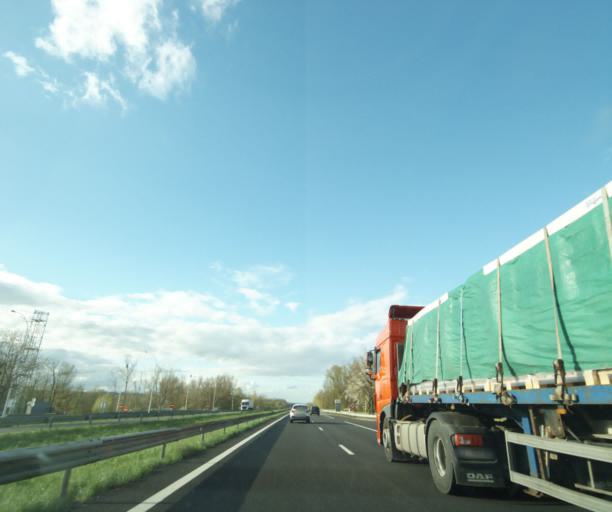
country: FR
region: Rhone-Alpes
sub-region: Departement du Rhone
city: Les Cheres
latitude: 45.9045
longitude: 4.7289
